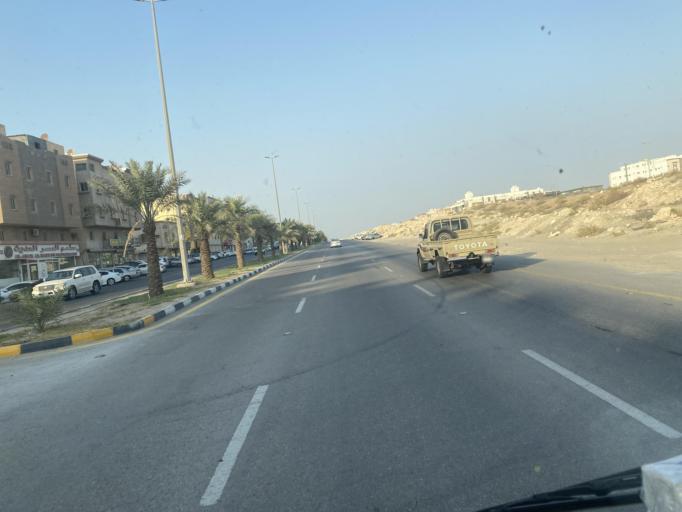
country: SA
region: Eastern Province
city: Dammam
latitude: 26.3584
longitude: 50.0638
